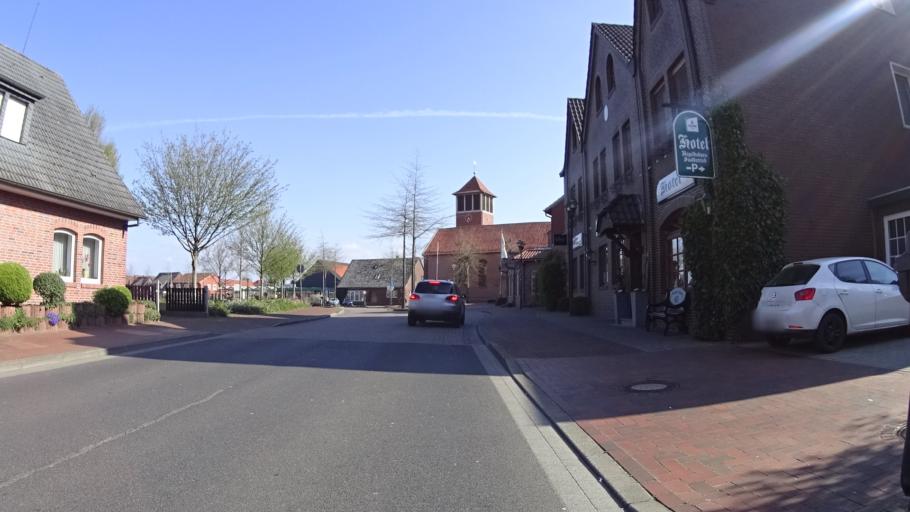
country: DE
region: Lower Saxony
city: Dorpen
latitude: 52.9662
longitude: 7.3216
